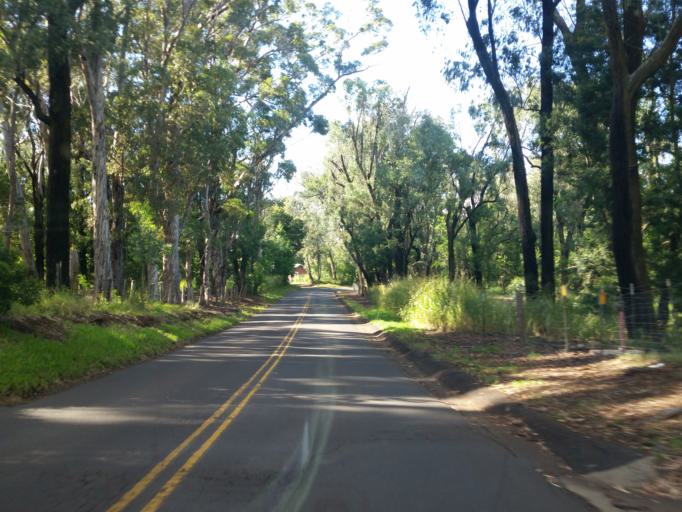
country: US
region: Hawaii
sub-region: Maui County
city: Pukalani
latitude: 20.8295
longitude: -156.3162
